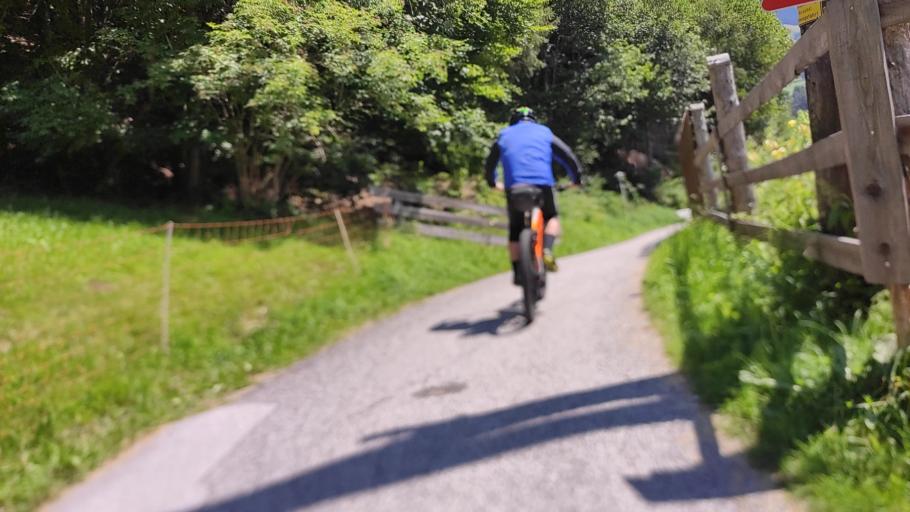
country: AT
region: Salzburg
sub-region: Politischer Bezirk Zell am See
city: Leogang
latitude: 47.4405
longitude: 12.7491
